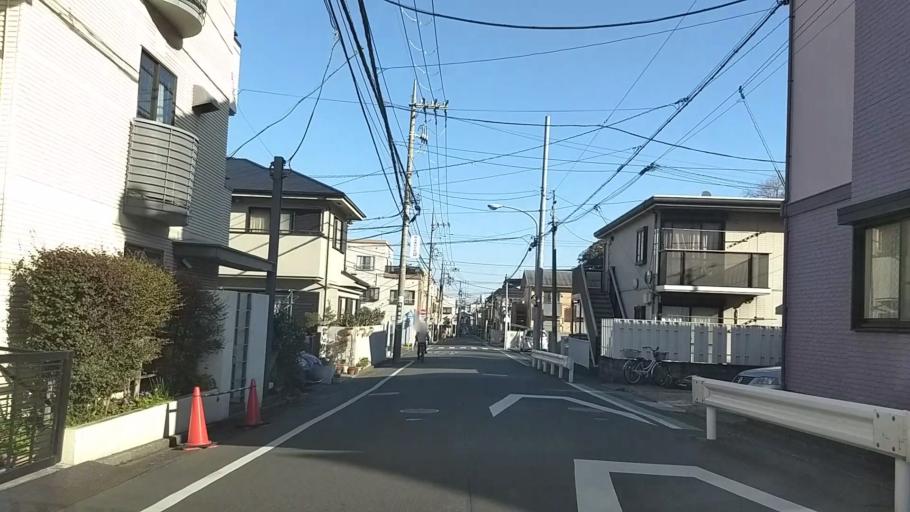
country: JP
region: Kanagawa
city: Yokohama
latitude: 35.4250
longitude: 139.6114
